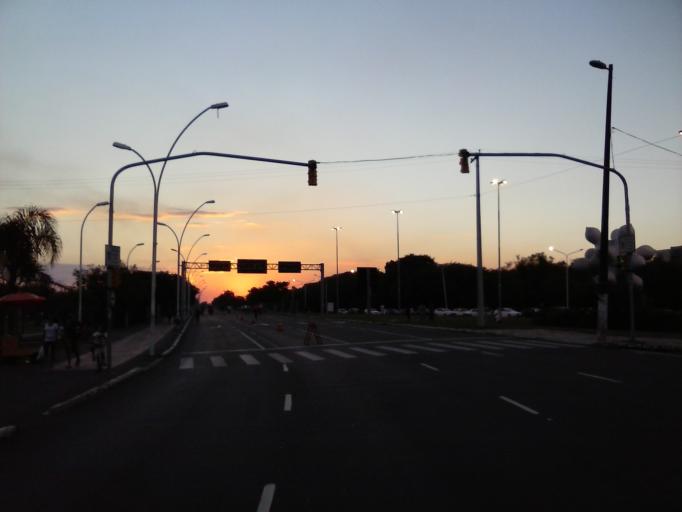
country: BR
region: Rio Grande do Sul
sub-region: Porto Alegre
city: Porto Alegre
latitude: -30.0428
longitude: -51.2335
